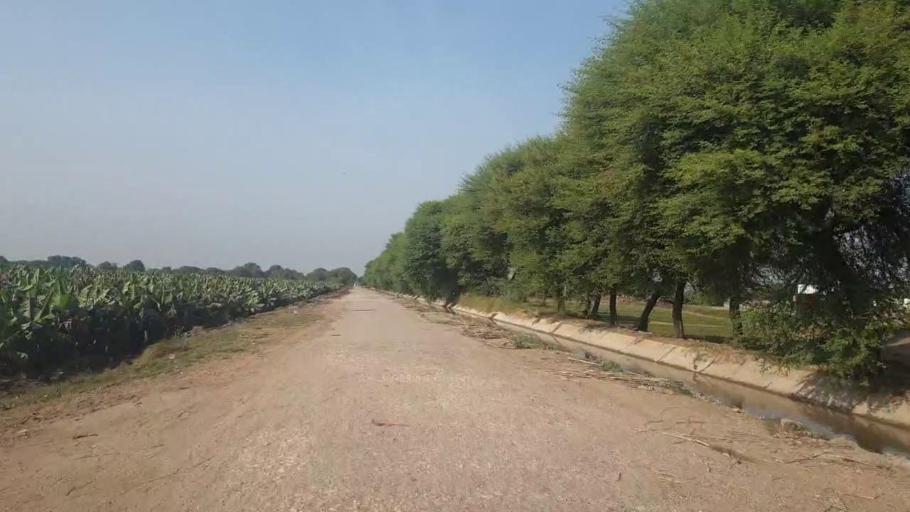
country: PK
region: Sindh
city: Tando Jam
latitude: 25.4163
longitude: 68.4641
